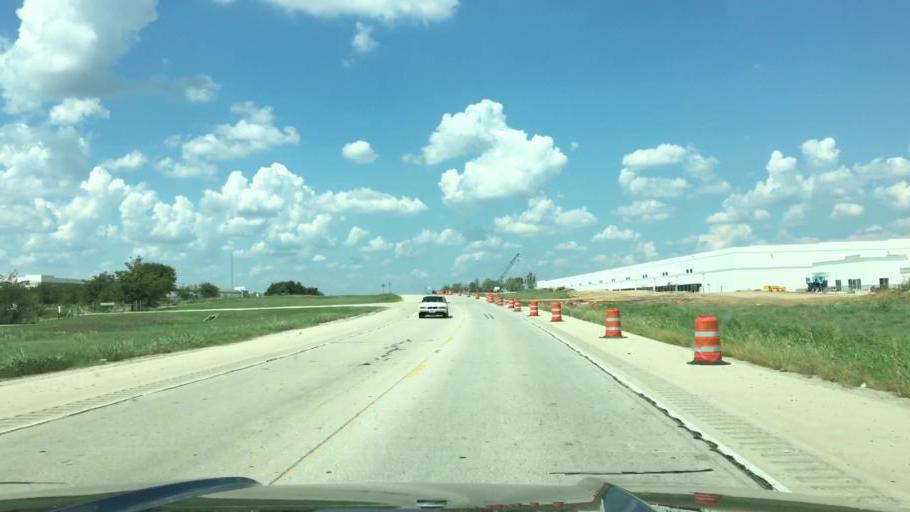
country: US
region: Texas
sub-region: Tarrant County
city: Haslet
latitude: 32.9830
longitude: -97.3419
